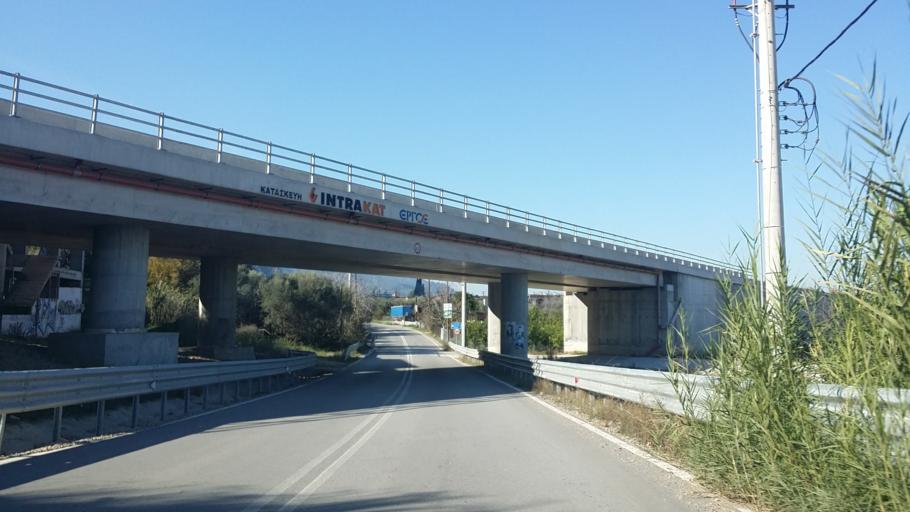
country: GR
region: West Greece
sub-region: Nomos Achaias
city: Temeni
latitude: 38.1826
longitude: 22.2079
